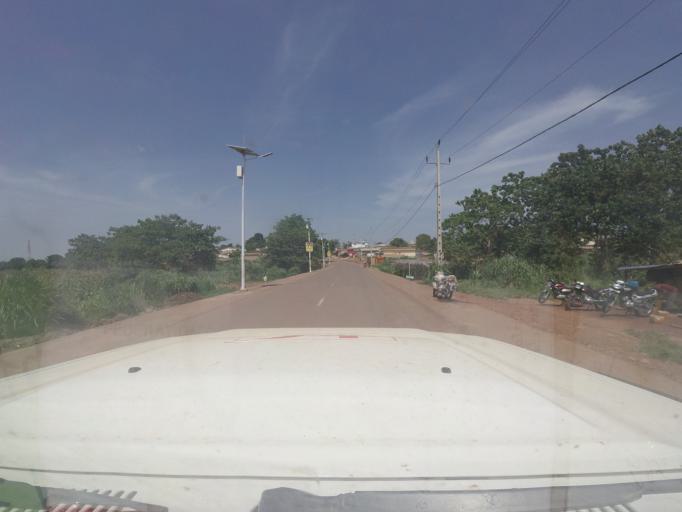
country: GN
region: Nzerekore
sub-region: Nzerekore Prefecture
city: Nzerekore
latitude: 7.7383
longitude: -8.8233
